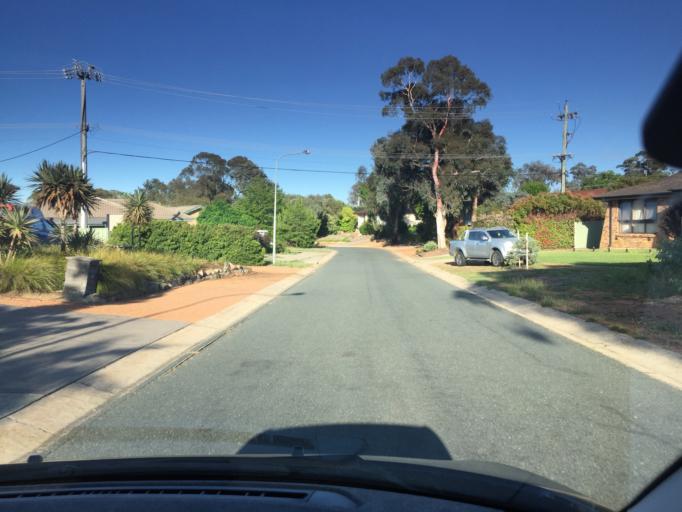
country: AU
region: Australian Capital Territory
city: Kaleen
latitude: -35.2191
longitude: 149.1133
